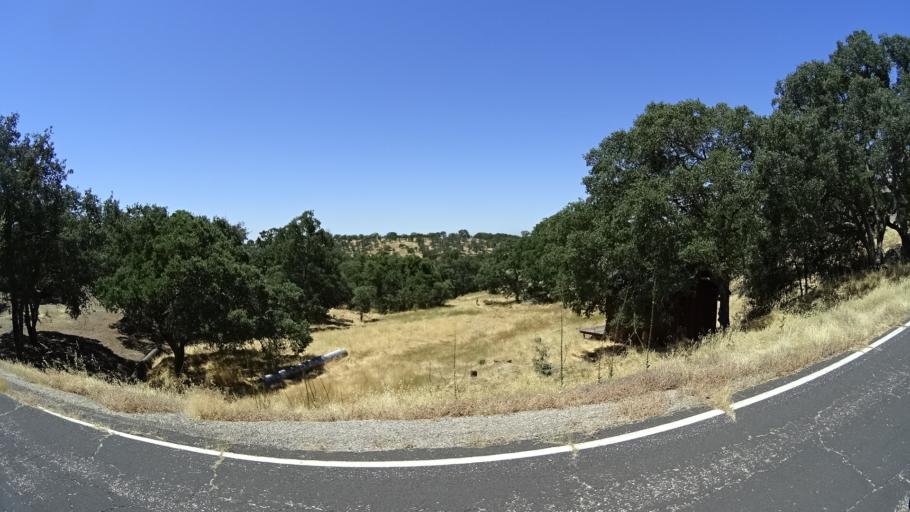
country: US
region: California
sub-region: Calaveras County
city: Rancho Calaveras
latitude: 38.1379
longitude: -120.8444
